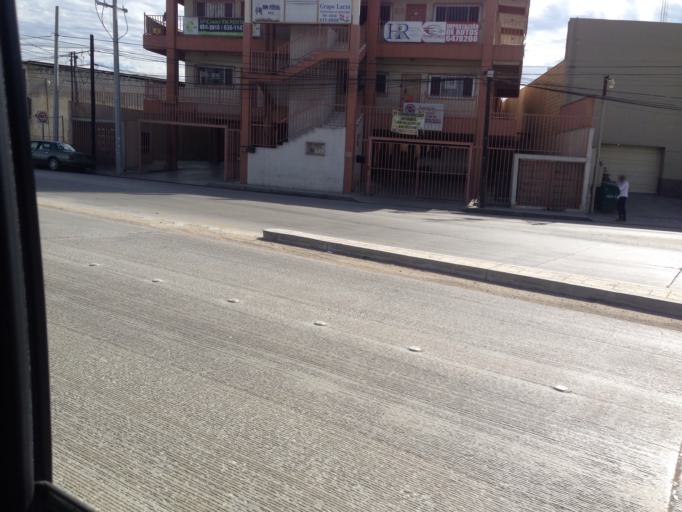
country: MX
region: Baja California
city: Tijuana
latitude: 32.5435
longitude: -116.9468
